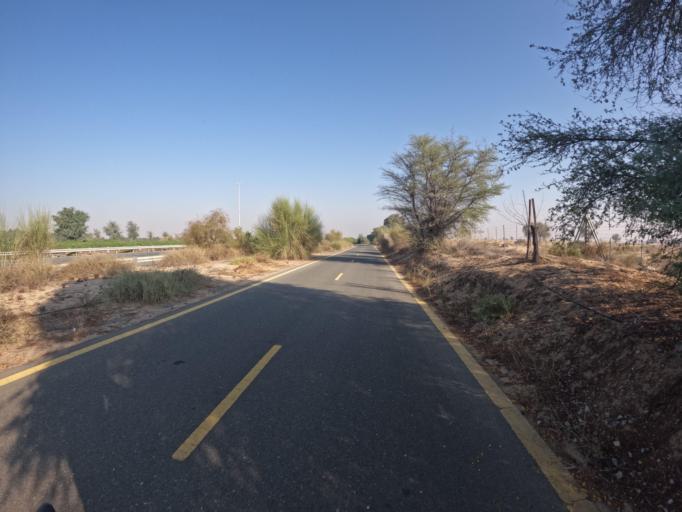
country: AE
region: Dubai
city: Dubai
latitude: 24.9012
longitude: 55.3418
